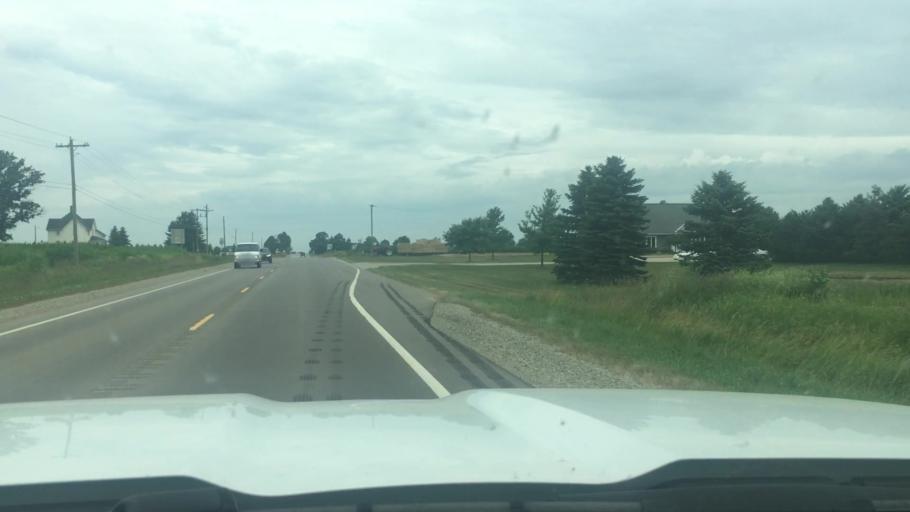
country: US
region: Michigan
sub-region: Clinton County
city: Fowler
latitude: 43.0017
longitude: -84.6977
